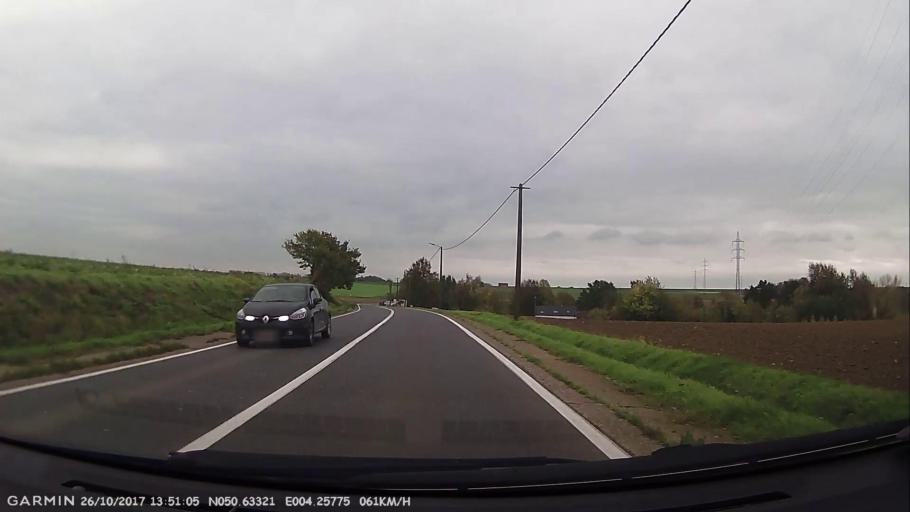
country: BE
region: Wallonia
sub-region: Province du Brabant Wallon
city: Ittre
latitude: 50.6331
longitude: 4.2580
